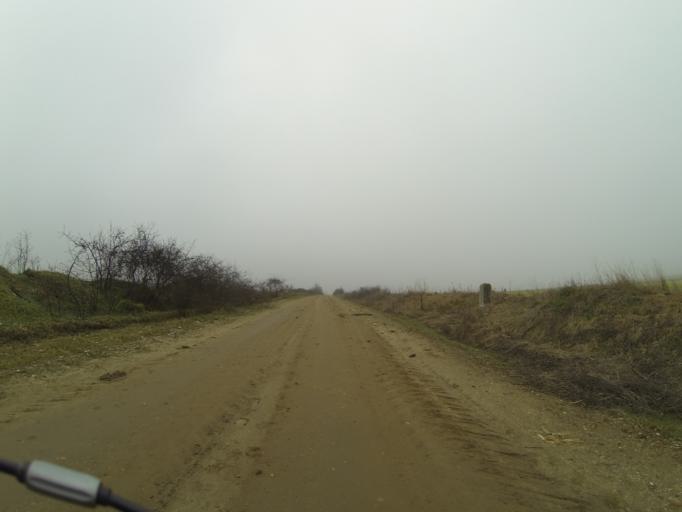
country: RO
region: Mehedinti
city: Dumbrava de Sus
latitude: 44.4824
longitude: 23.0607
